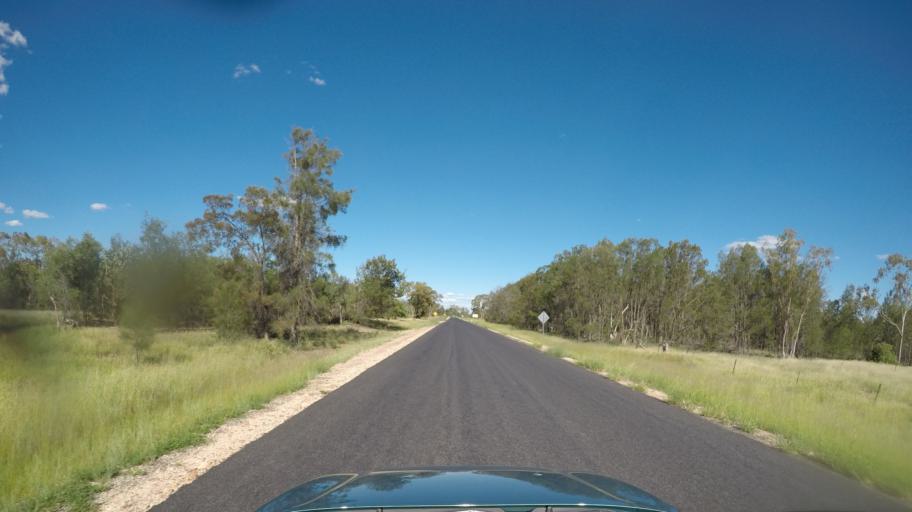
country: AU
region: Queensland
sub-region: Goondiwindi
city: Goondiwindi
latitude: -28.1705
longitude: 150.4719
